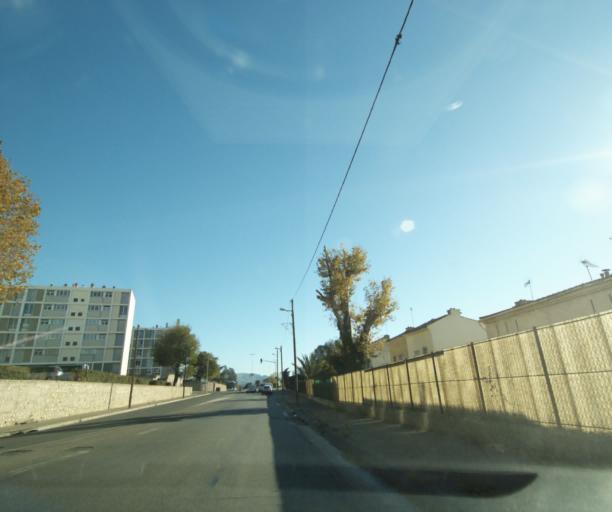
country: FR
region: Provence-Alpes-Cote d'Azur
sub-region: Departement des Bouches-du-Rhone
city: Marseille 14
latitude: 43.3504
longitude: 5.3744
